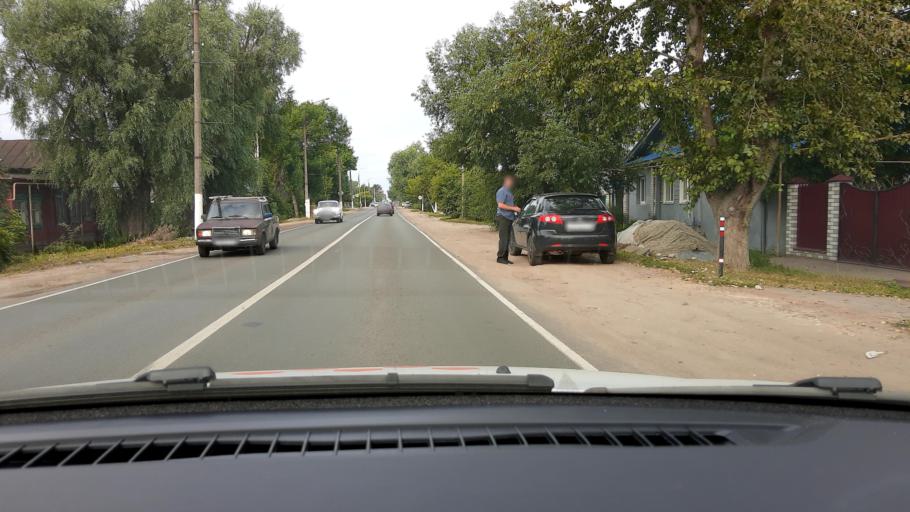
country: RU
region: Nizjnij Novgorod
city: Vyyezdnoye
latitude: 55.3837
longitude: 43.7937
